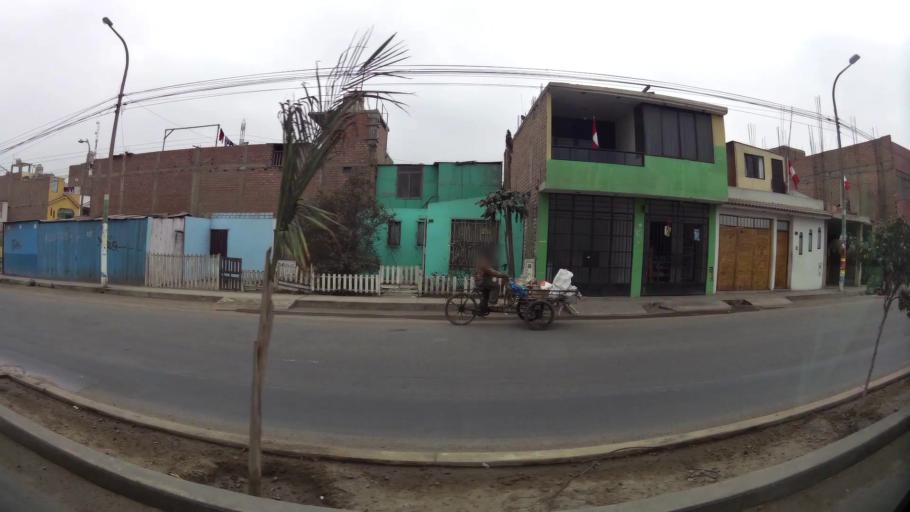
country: PE
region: Lima
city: Ventanilla
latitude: -11.9303
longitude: -77.0797
